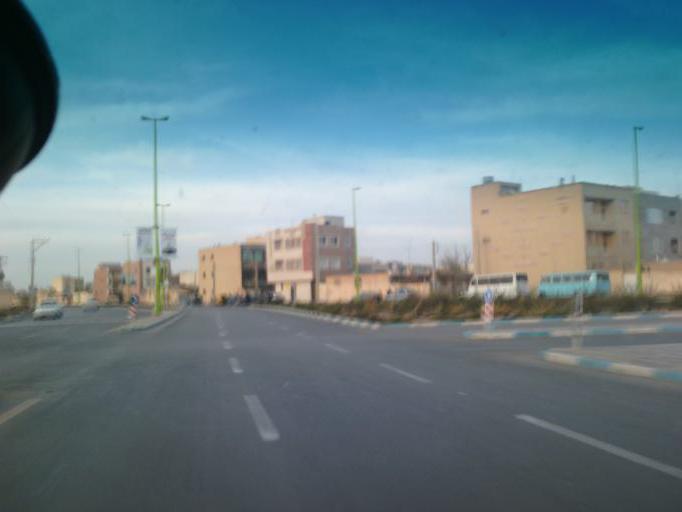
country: IR
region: Isfahan
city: Shahin Shahr
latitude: 32.8697
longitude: 51.5422
